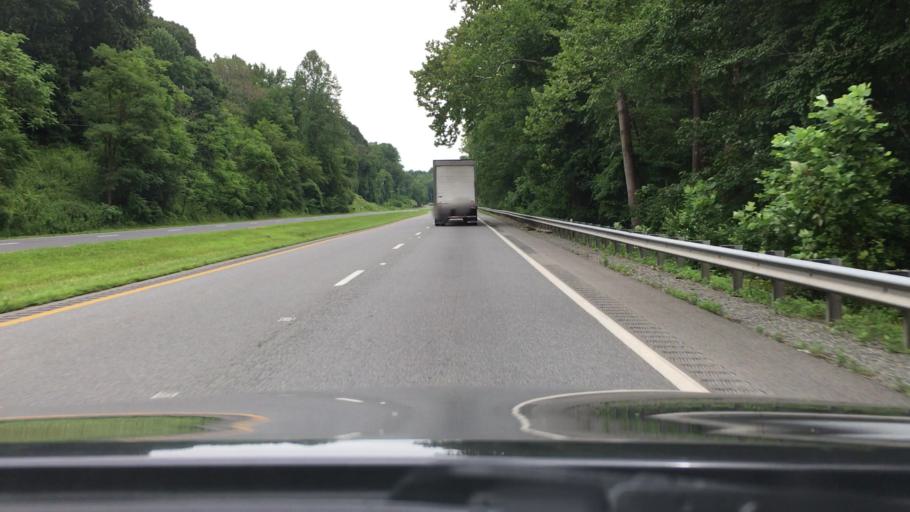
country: US
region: Virginia
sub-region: City of Charlottesville
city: Charlottesville
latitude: 38.0109
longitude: -78.5601
